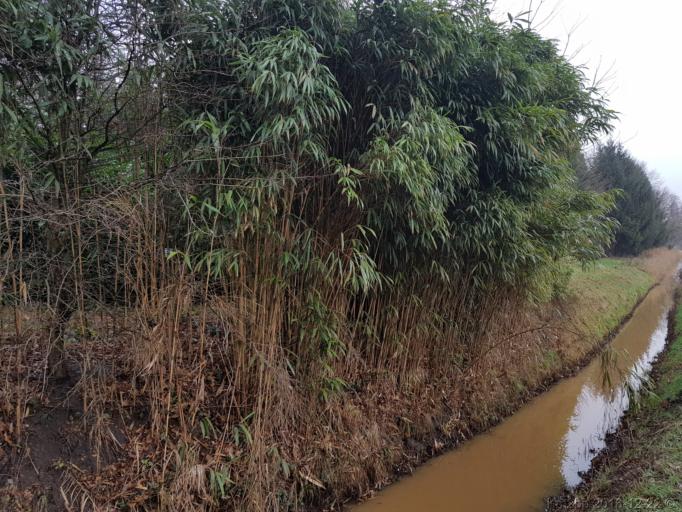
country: NL
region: North Brabant
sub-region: Gemeente Breda
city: Hoge Vucht
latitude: 51.6300
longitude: 4.7778
